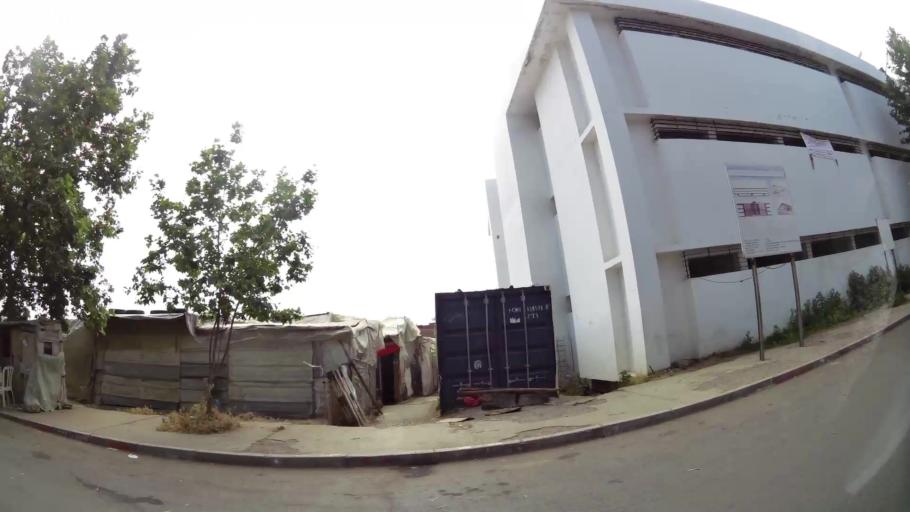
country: MA
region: Gharb-Chrarda-Beni Hssen
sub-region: Kenitra Province
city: Kenitra
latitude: 34.2611
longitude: -6.5710
